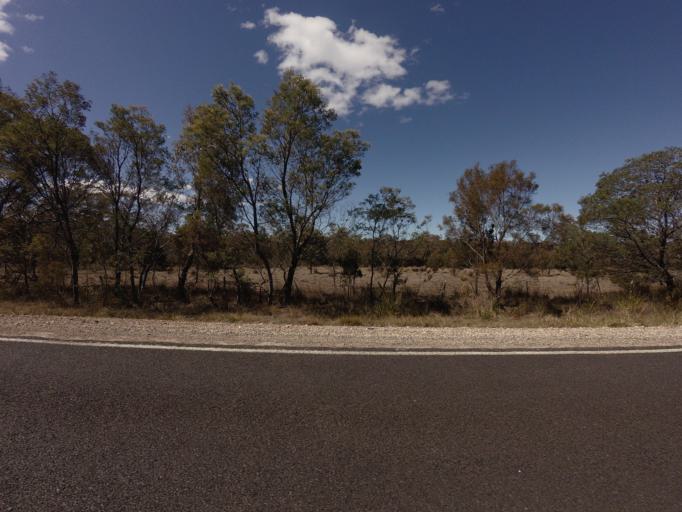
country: AU
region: Tasmania
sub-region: Break O'Day
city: St Helens
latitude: -42.0367
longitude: 148.0267
